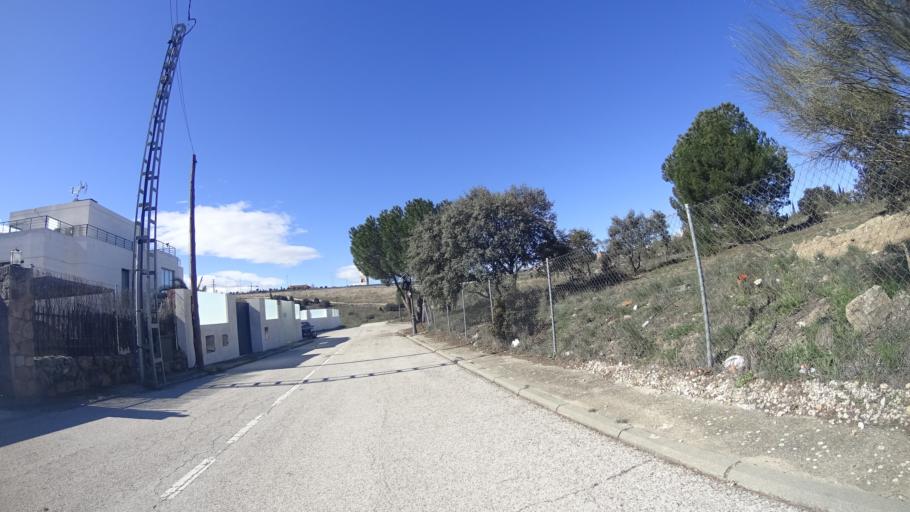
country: ES
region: Madrid
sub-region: Provincia de Madrid
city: Torrelodones
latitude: 40.5721
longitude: -3.9167
